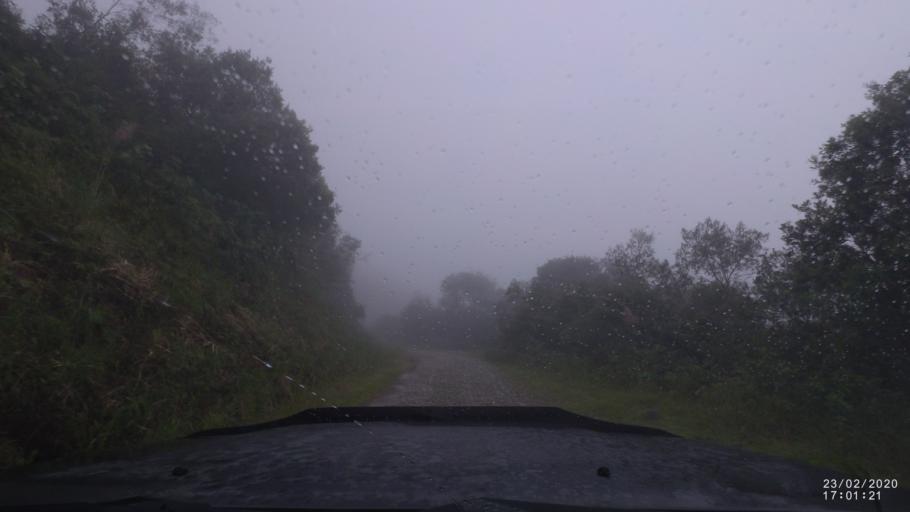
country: BO
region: Cochabamba
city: Colomi
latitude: -17.1126
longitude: -65.9658
